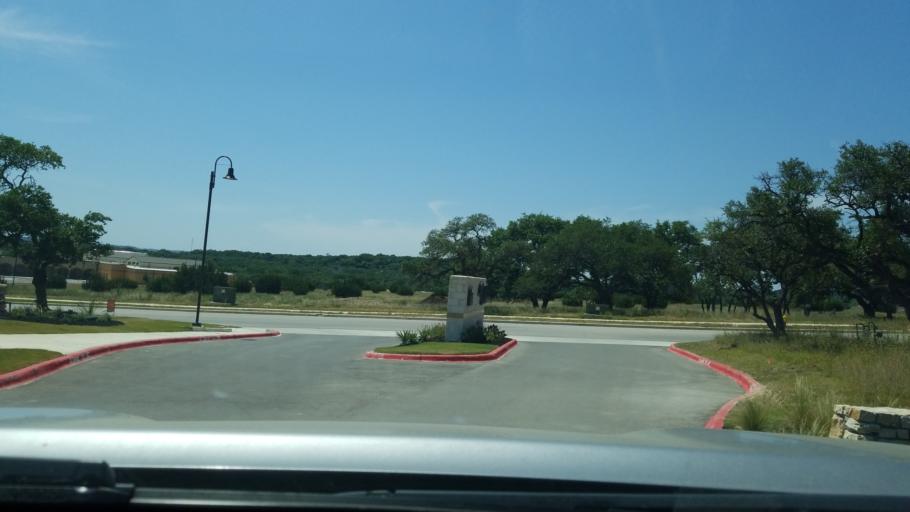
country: US
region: Texas
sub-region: Kendall County
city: Boerne
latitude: 29.8060
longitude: -98.6919
